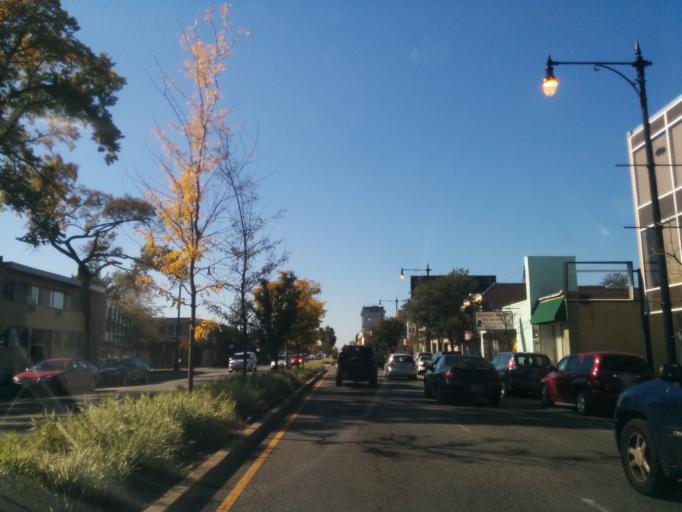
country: US
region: Illinois
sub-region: Cook County
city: Elmwood Park
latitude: 41.9090
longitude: -87.8005
